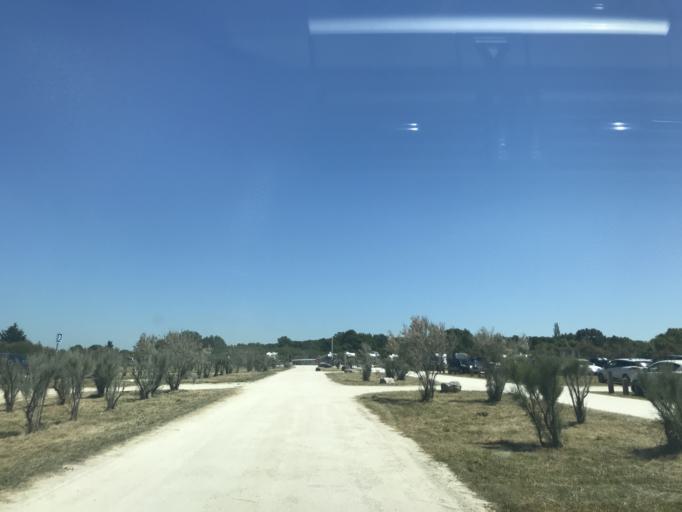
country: FR
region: Poitou-Charentes
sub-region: Departement de la Charente-Maritime
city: Meschers-sur-Gironde
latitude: 45.5369
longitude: -0.9040
